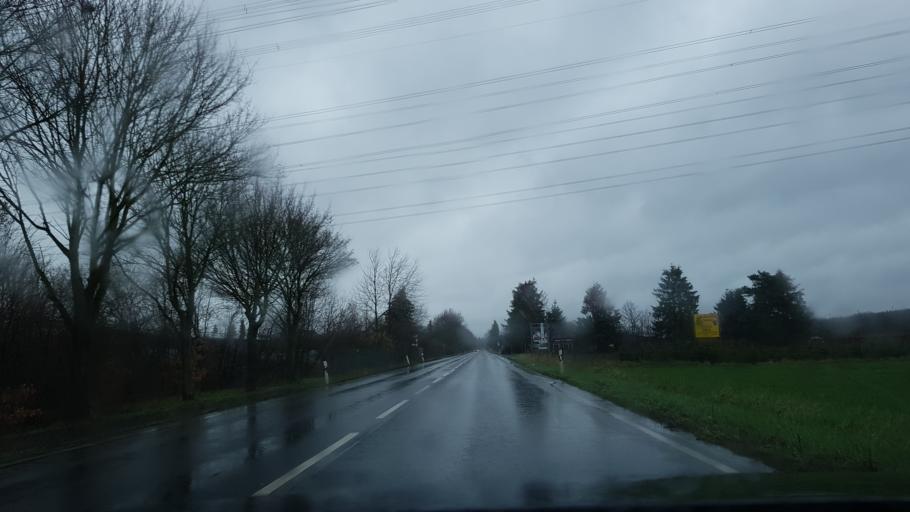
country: DE
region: North Rhine-Westphalia
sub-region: Regierungsbezirk Dusseldorf
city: Langenfeld
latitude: 51.1257
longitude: 6.9188
